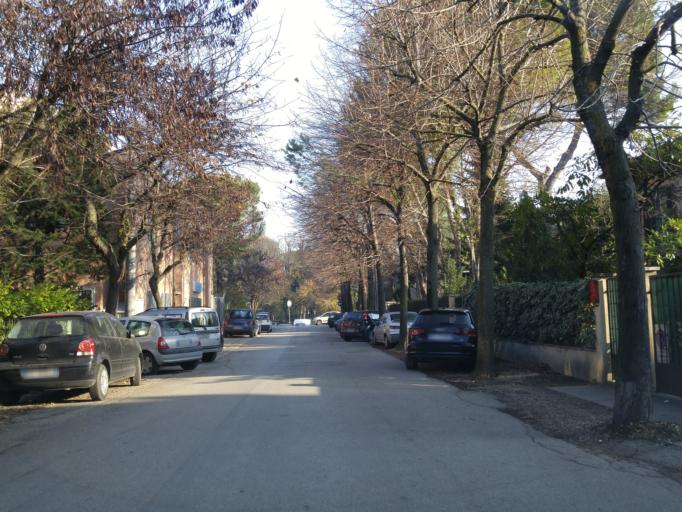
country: IT
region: The Marches
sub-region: Provincia di Pesaro e Urbino
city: Fano
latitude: 43.8387
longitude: 13.0112
